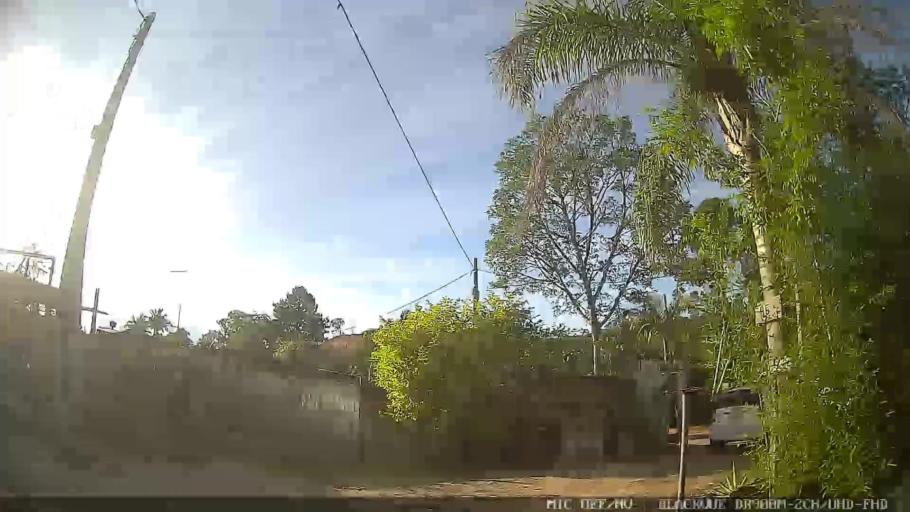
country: BR
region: Sao Paulo
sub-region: Mogi das Cruzes
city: Mogi das Cruzes
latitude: -23.5115
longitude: -46.1304
